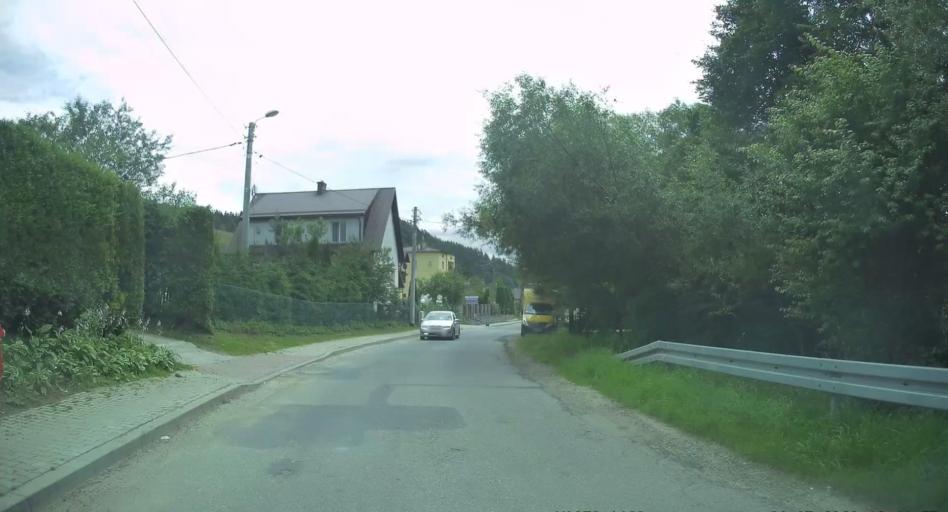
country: PL
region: Lesser Poland Voivodeship
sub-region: Powiat nowosadecki
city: Muszyna
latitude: 49.3689
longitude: 20.8892
